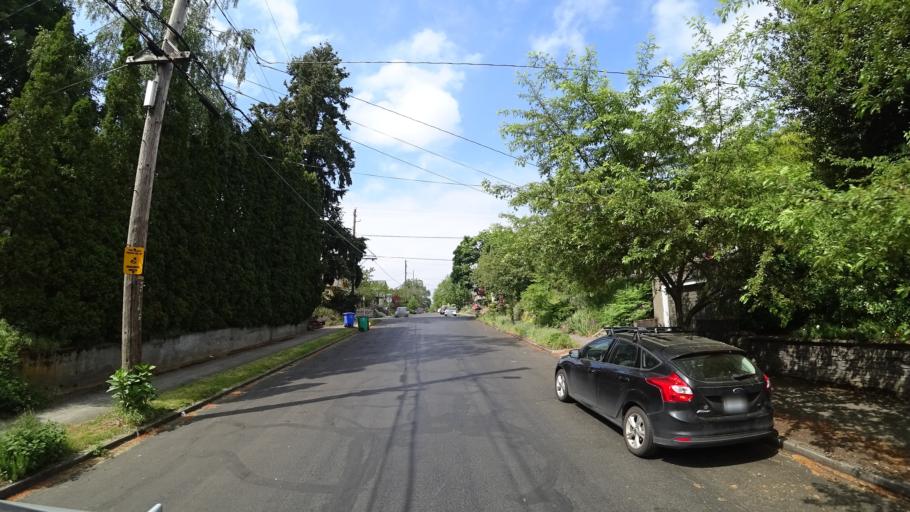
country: US
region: Oregon
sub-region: Multnomah County
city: Portland
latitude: 45.5551
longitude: -122.6518
